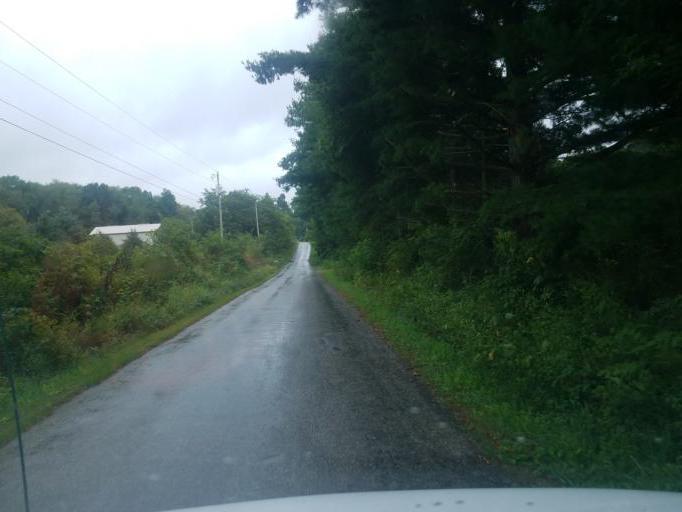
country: US
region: Ohio
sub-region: Wayne County
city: West Salem
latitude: 40.9186
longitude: -82.1531
